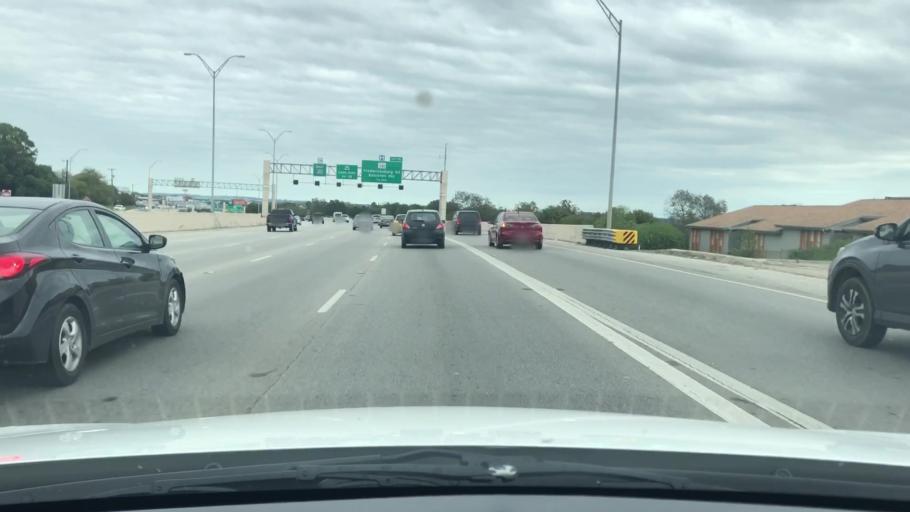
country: US
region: Texas
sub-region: Bexar County
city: Balcones Heights
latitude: 29.4892
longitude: -98.5648
